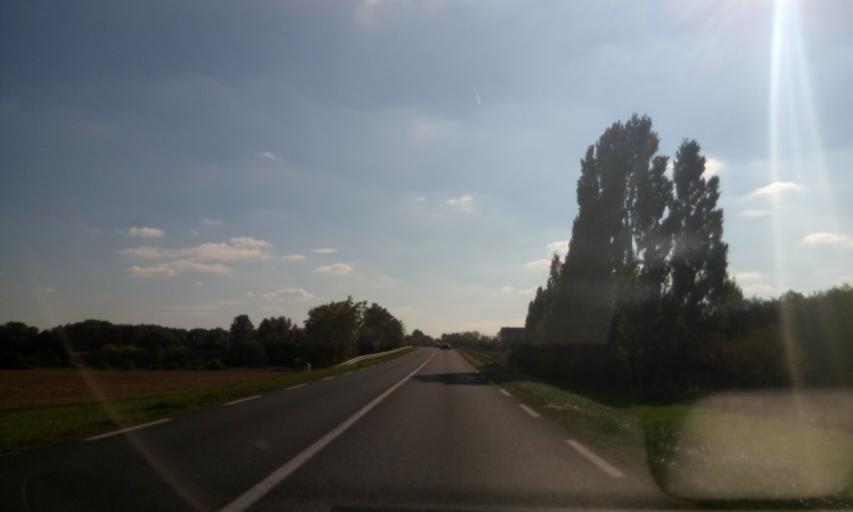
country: FR
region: Centre
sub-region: Departement d'Indre-et-Loire
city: Poce-sur-Cisse
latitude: 47.4353
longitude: 1.0068
